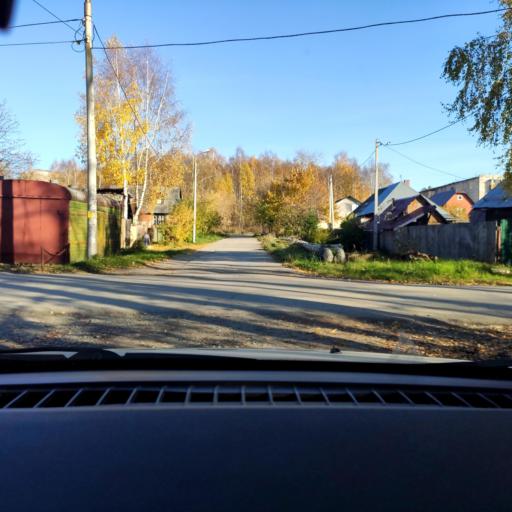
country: RU
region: Perm
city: Perm
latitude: 58.0786
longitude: 56.3567
